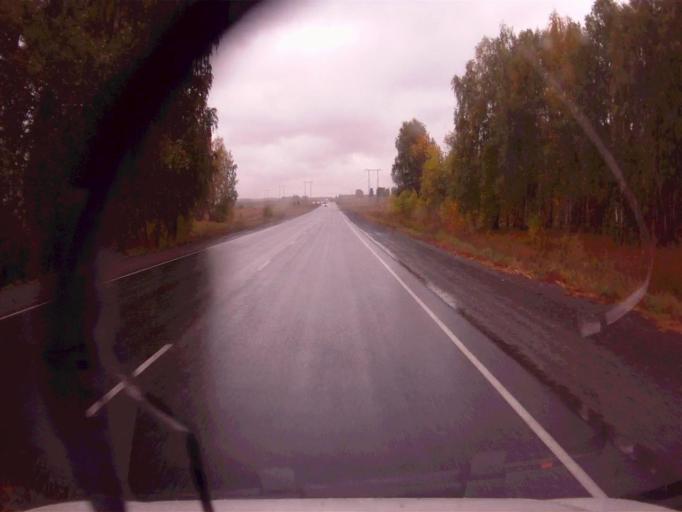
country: RU
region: Chelyabinsk
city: Roshchino
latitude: 55.3878
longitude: 61.1284
